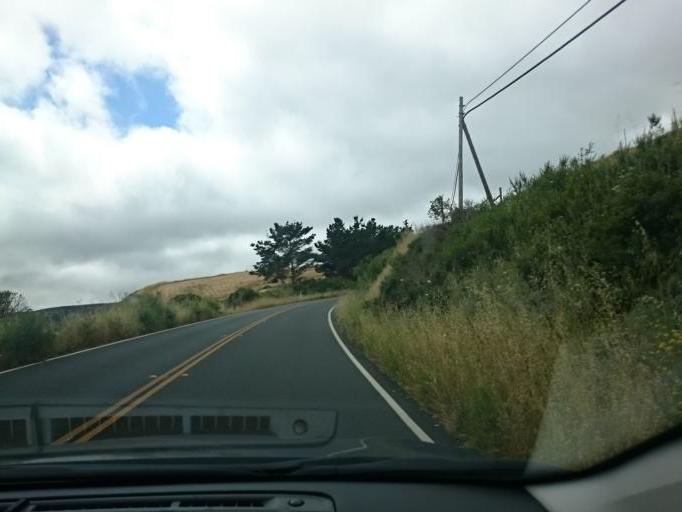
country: US
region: California
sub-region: Marin County
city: Inverness
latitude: 38.1491
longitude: -122.8854
